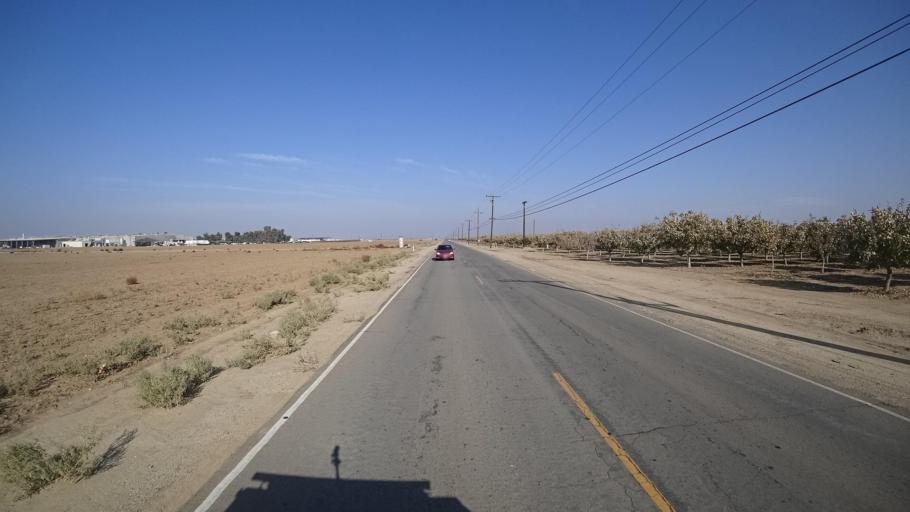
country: US
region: California
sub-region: Kern County
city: McFarland
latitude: 35.6992
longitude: -119.2242
